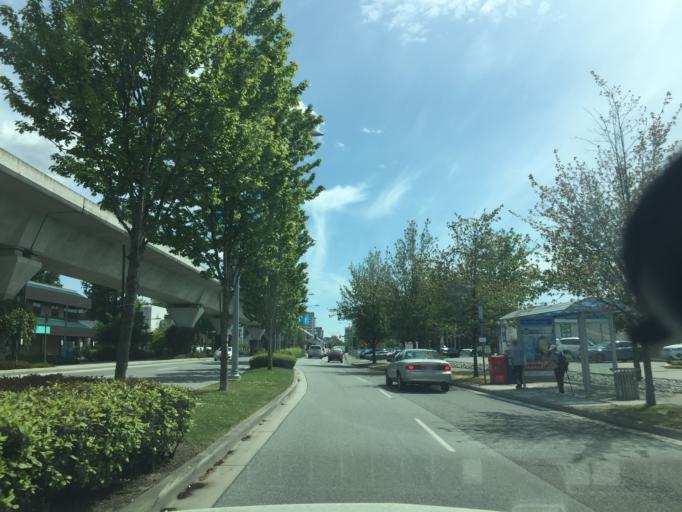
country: CA
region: British Columbia
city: Richmond
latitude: 49.1795
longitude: -123.1368
